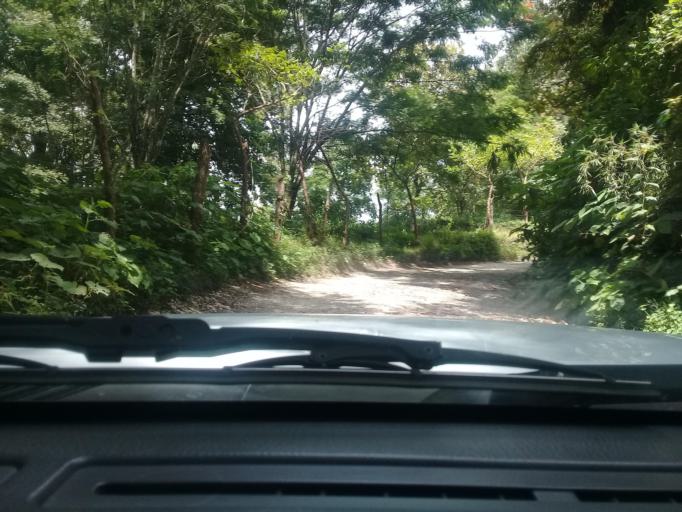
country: MX
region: Veracruz
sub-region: Tlalnelhuayocan
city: Guadalupe Victoria
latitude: 19.5489
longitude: -96.9639
